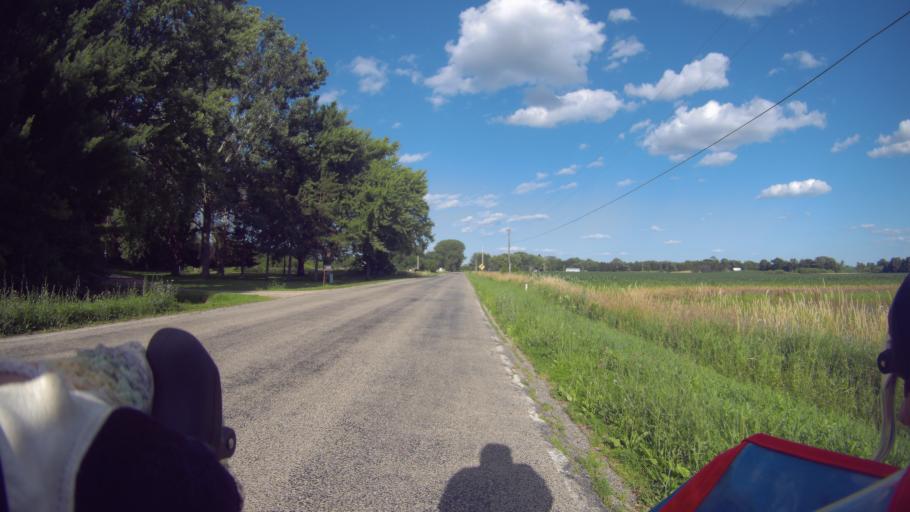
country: US
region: Wisconsin
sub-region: Dane County
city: Oregon
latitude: 42.9350
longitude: -89.3411
